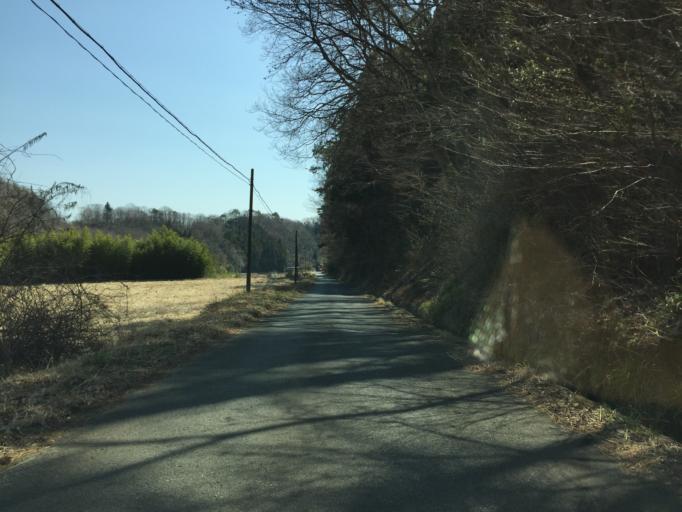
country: JP
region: Fukushima
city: Iwaki
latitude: 37.0090
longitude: 140.7918
